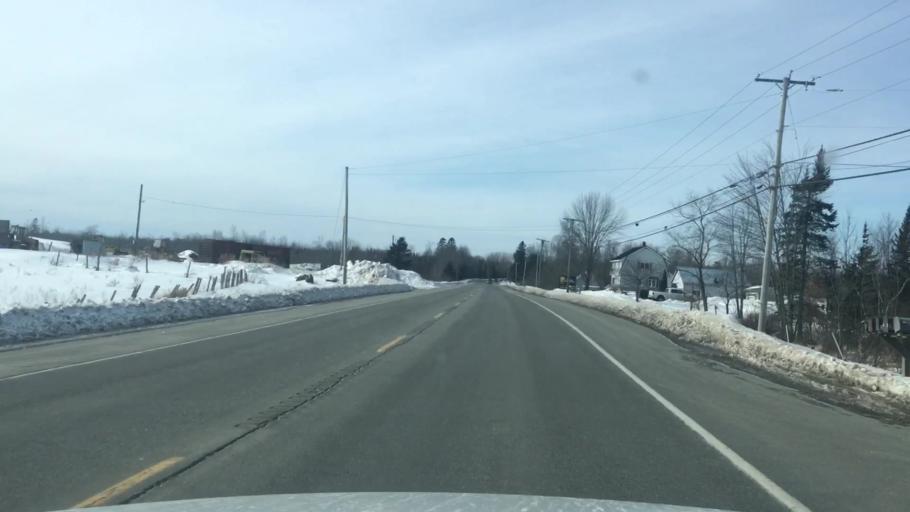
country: US
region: Maine
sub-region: Penobscot County
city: Kenduskeag
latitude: 44.9045
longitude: -68.8894
